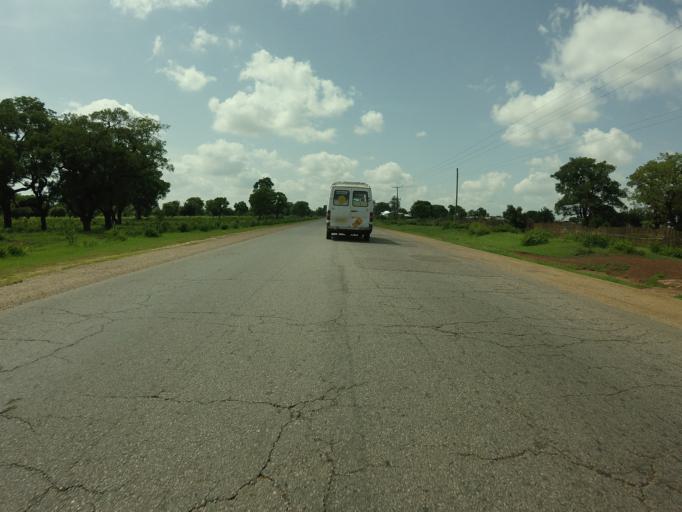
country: GH
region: Northern
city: Savelugu
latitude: 9.5750
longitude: -0.8345
